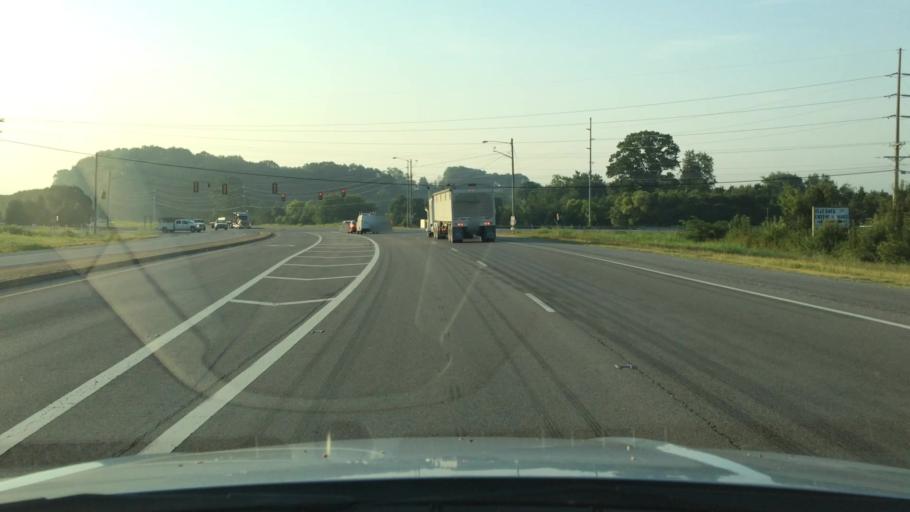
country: US
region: Tennessee
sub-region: Giles County
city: Pulaski
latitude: 35.1713
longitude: -87.0562
